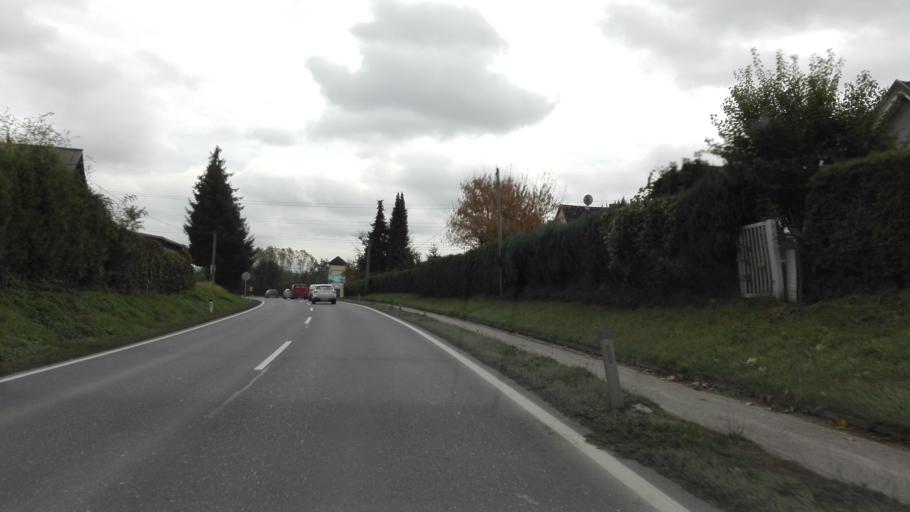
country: AT
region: Upper Austria
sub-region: Politischer Bezirk Urfahr-Umgebung
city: Feldkirchen an der Donau
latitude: 48.2945
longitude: 14.0361
